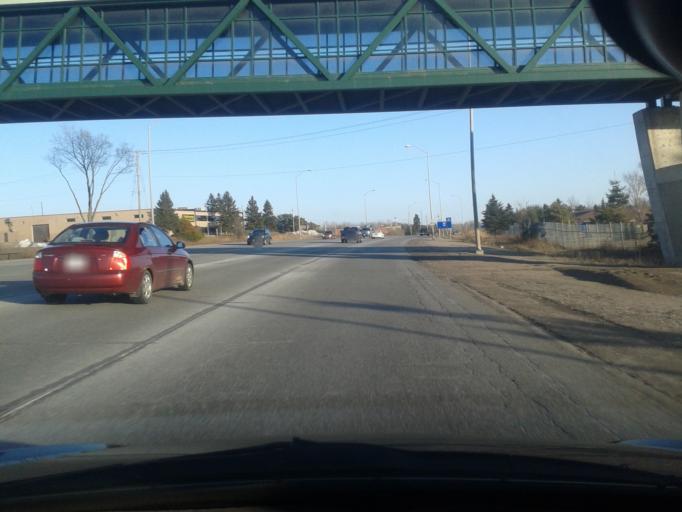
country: CA
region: Ontario
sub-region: Nipissing District
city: North Bay
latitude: 46.3256
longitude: -79.4497
